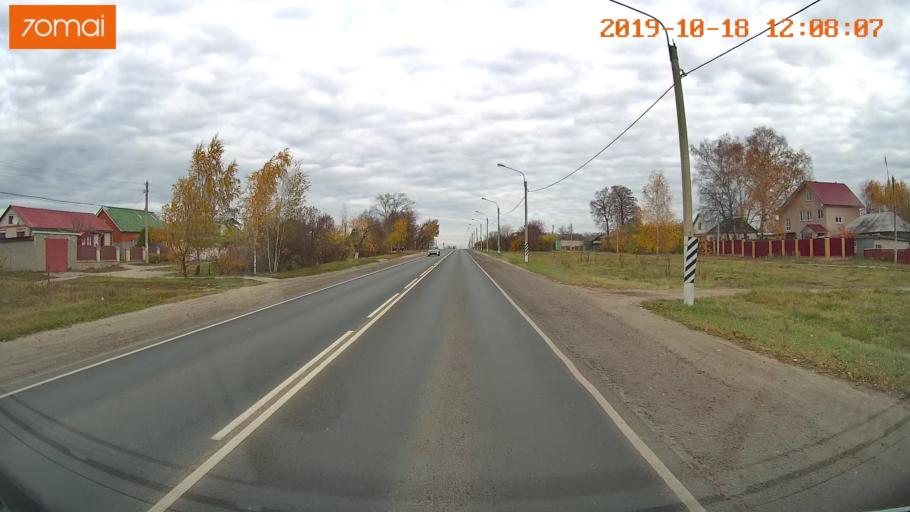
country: RU
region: Rjazan
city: Zakharovo
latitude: 54.3728
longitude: 39.2883
